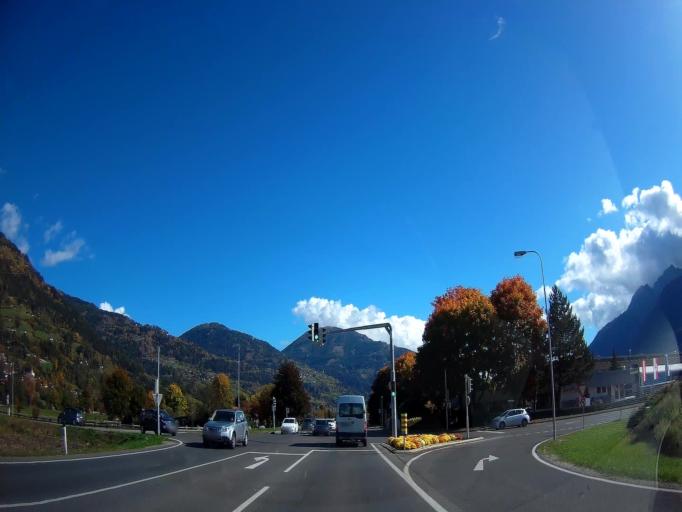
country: AT
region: Tyrol
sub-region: Politischer Bezirk Lienz
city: Tristach
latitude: 46.8306
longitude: 12.7932
